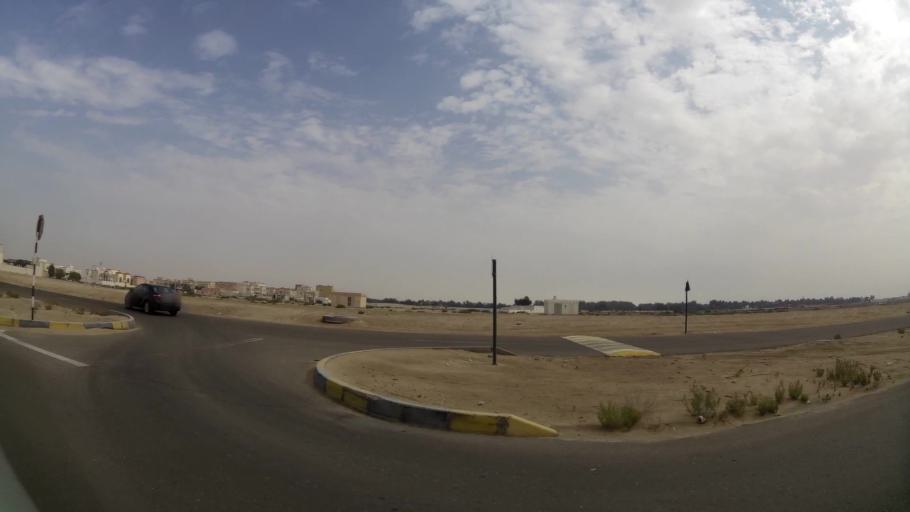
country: AE
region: Abu Dhabi
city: Abu Dhabi
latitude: 24.3041
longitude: 54.6581
